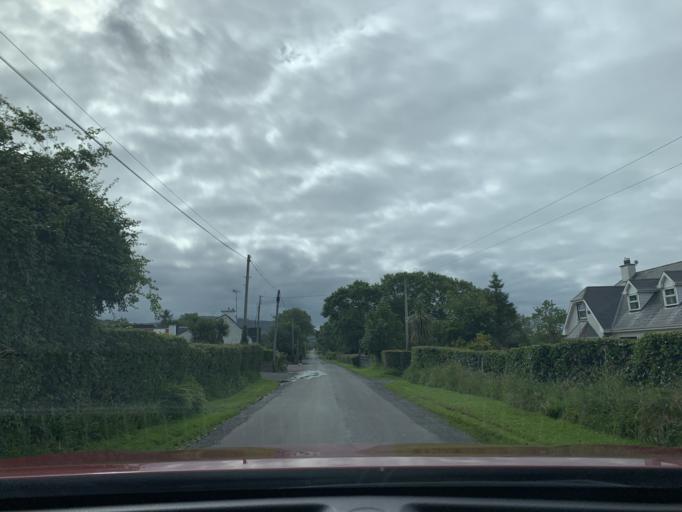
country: IE
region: Connaught
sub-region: Sligo
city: Sligo
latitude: 54.3415
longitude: -8.4838
